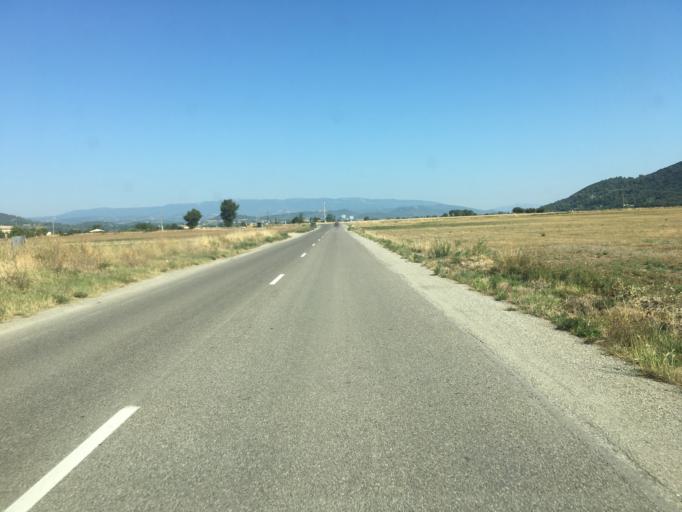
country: FR
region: Provence-Alpes-Cote d'Azur
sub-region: Departement des Alpes-de-Haute-Provence
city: Oraison
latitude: 43.8827
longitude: 5.9089
